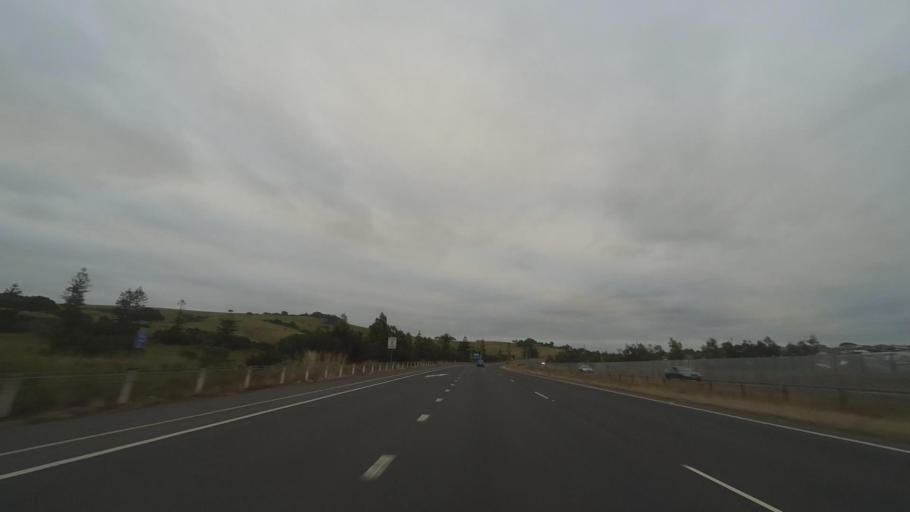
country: AU
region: New South Wales
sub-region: Shellharbour
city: Croom
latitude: -34.5834
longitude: 150.8405
